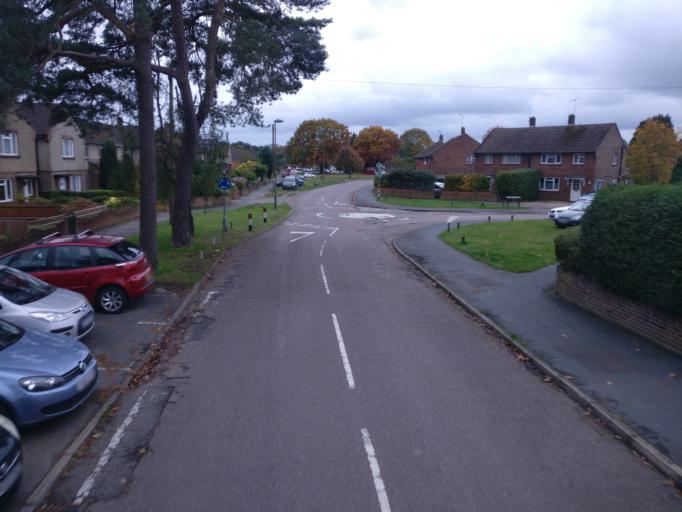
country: GB
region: England
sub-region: Surrey
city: Camberley
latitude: 51.3474
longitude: -0.7284
